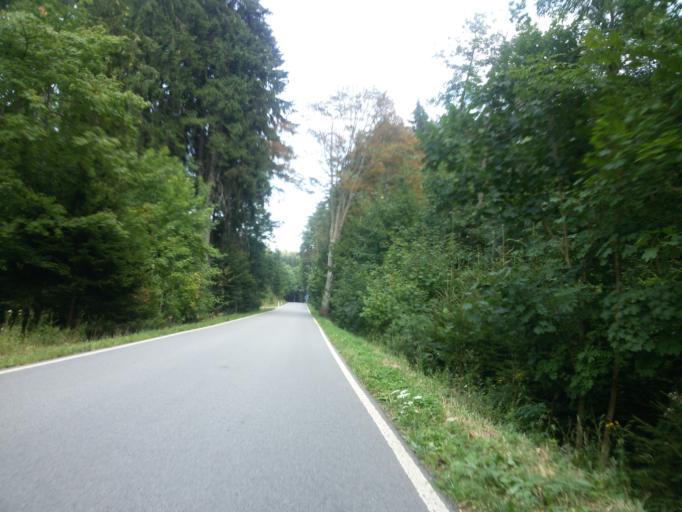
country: CZ
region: South Moravian
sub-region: Okres Brno-Venkov
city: Lomnice
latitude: 49.4642
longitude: 16.4530
